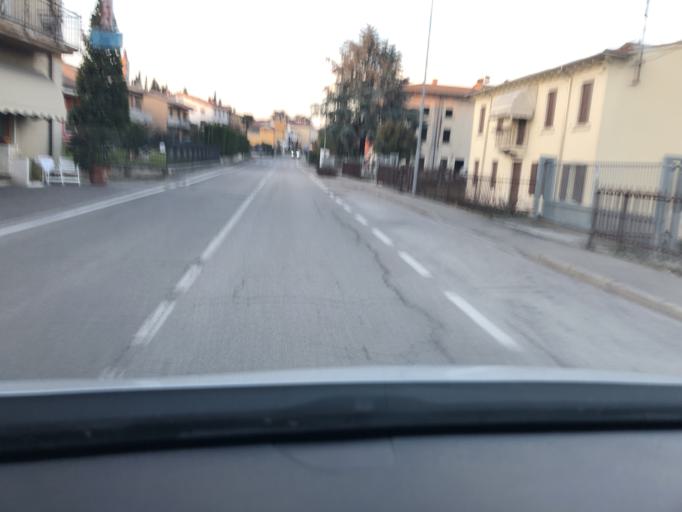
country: IT
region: Veneto
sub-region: Provincia di Verona
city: Sommacampagna
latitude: 45.4031
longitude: 10.8458
